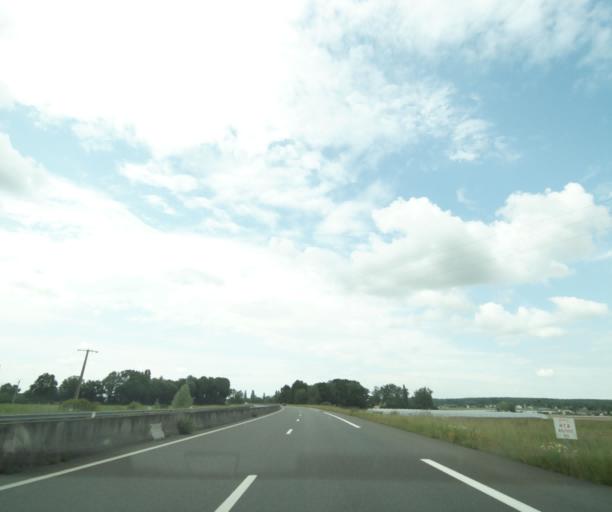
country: FR
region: Pays de la Loire
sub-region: Departement de Maine-et-Loire
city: Vivy
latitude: 47.3282
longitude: -0.0356
